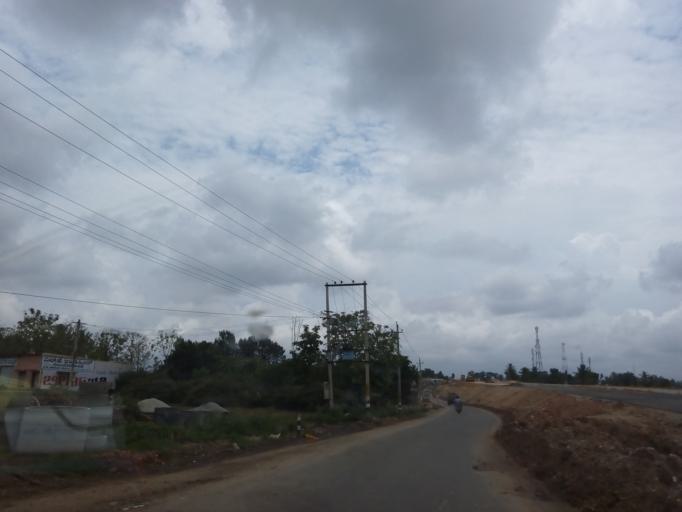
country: IN
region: Karnataka
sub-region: Hassan
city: Hassan
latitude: 12.9852
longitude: 76.2215
